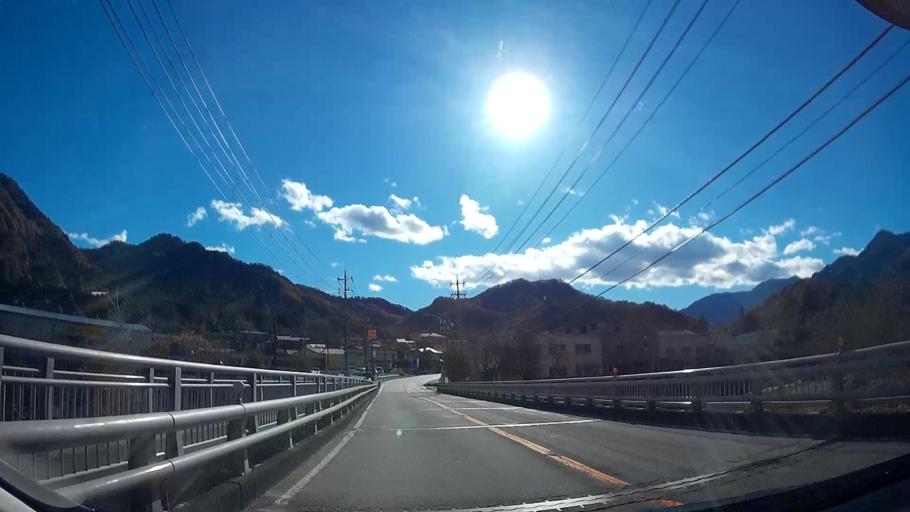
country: JP
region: Yamanashi
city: Otsuki
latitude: 35.5982
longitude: 138.8890
